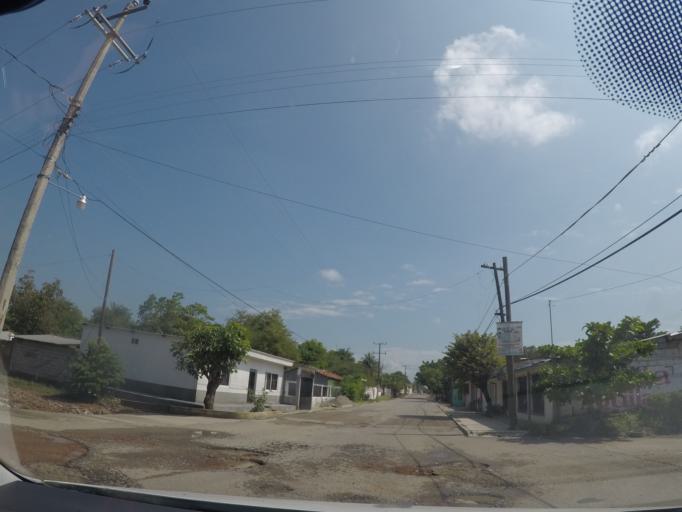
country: MX
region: Oaxaca
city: San Francisco Ixhuatan
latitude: 16.3958
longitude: -94.4584
